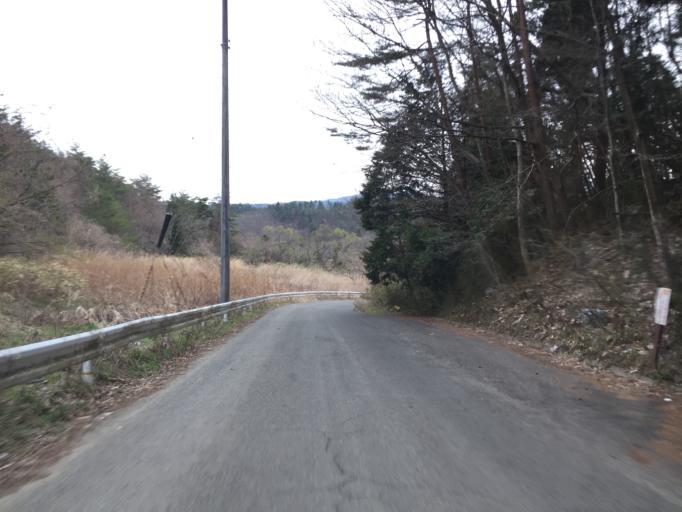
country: JP
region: Fukushima
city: Fukushima-shi
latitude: 37.7203
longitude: 140.4171
